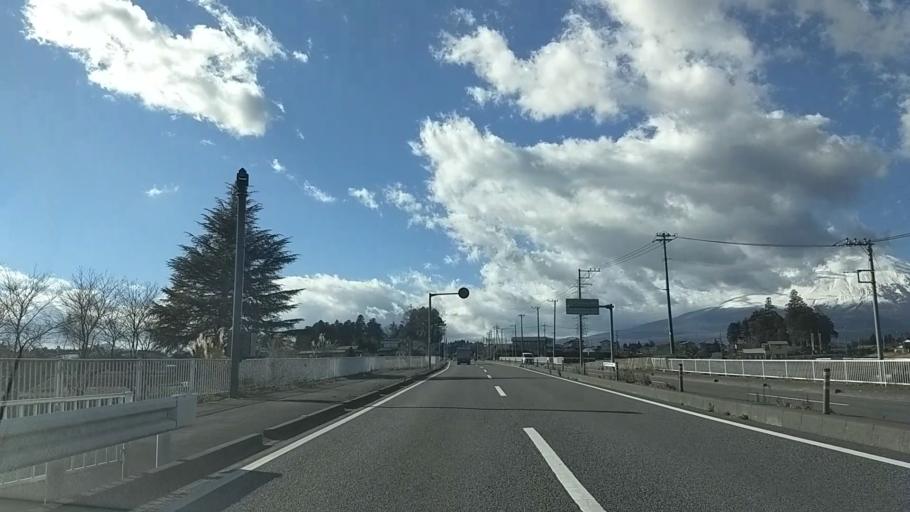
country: JP
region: Shizuoka
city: Gotemba
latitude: 35.3384
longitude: 138.9418
